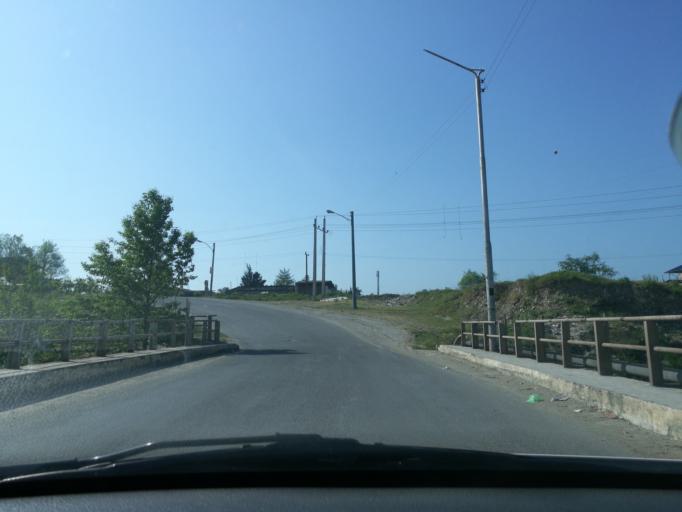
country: IR
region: Mazandaran
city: Chalus
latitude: 36.6594
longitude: 51.4366
